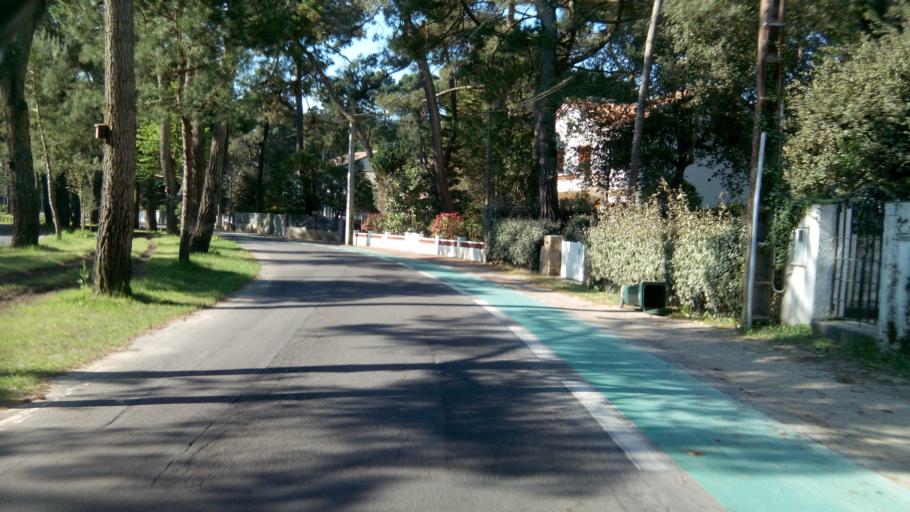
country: FR
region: Pays de la Loire
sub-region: Departement de la Loire-Atlantique
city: La Baule-Escoublac
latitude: 47.2830
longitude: -2.3763
